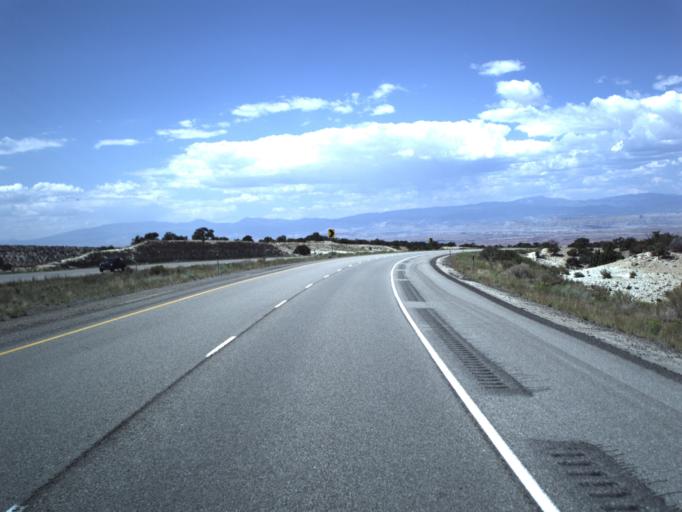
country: US
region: Utah
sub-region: Emery County
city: Ferron
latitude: 38.8487
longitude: -110.9313
